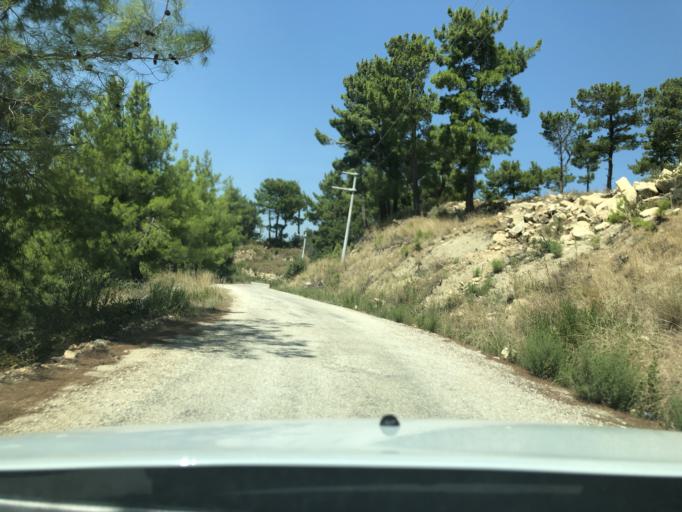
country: TR
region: Antalya
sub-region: Manavgat
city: Manavgat
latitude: 36.8711
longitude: 31.5533
